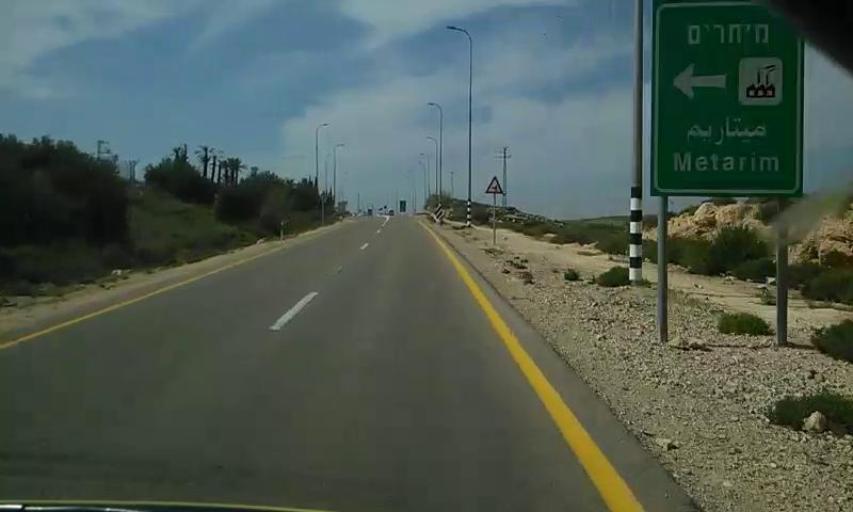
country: PS
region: West Bank
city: Az Zahiriyah
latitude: 31.3752
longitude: 35.0087
